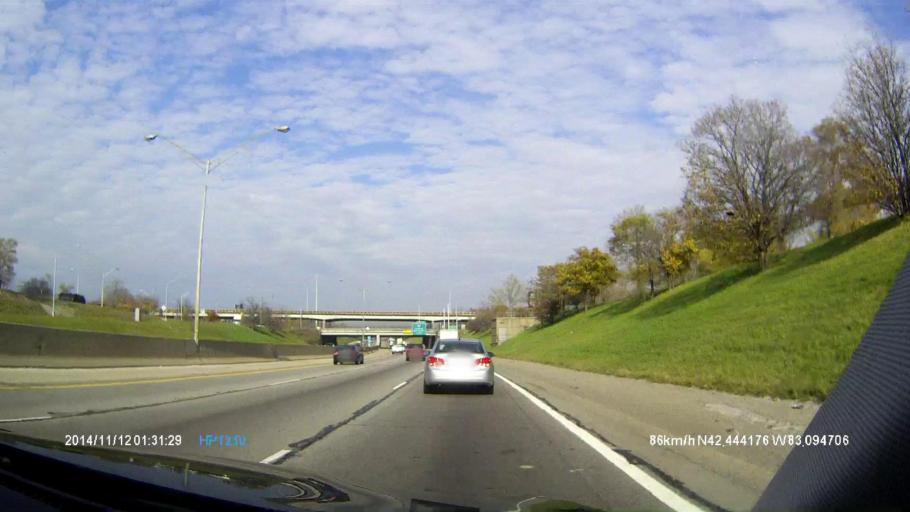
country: US
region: Michigan
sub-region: Oakland County
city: Hazel Park
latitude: 42.4442
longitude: -83.0947
